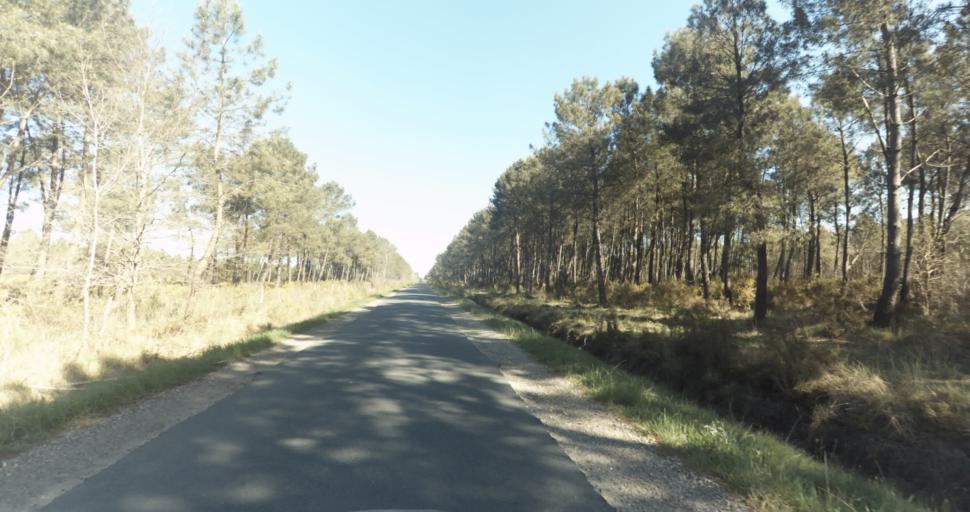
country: FR
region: Aquitaine
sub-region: Departement de la Gironde
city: Marcheprime
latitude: 44.7567
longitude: -0.8508
